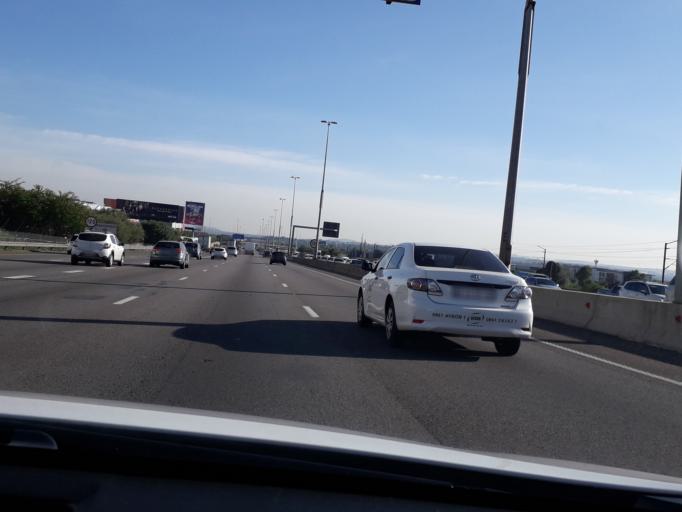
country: ZA
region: Gauteng
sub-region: City of Tshwane Metropolitan Municipality
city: Centurion
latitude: -25.8901
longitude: 28.1656
